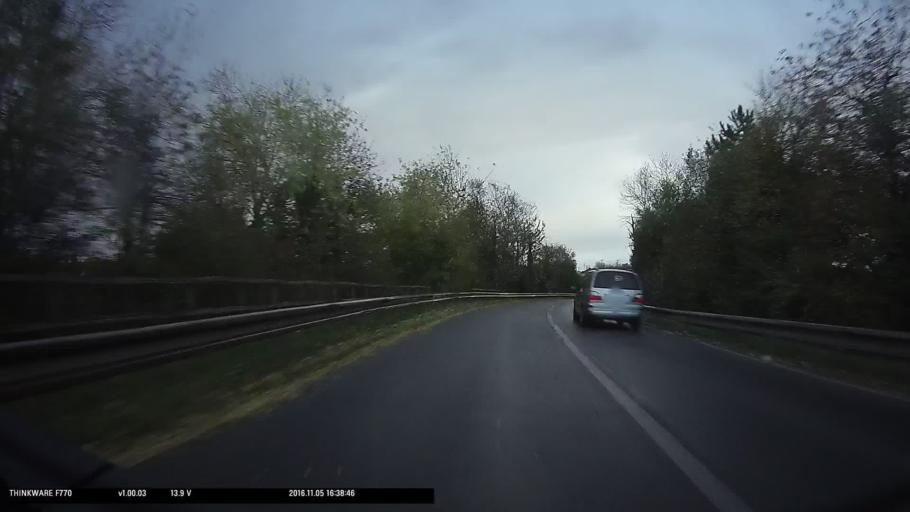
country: FR
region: Ile-de-France
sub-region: Departement du Val-d'Oise
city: Vaureal
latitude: 49.0603
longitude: 2.0194
